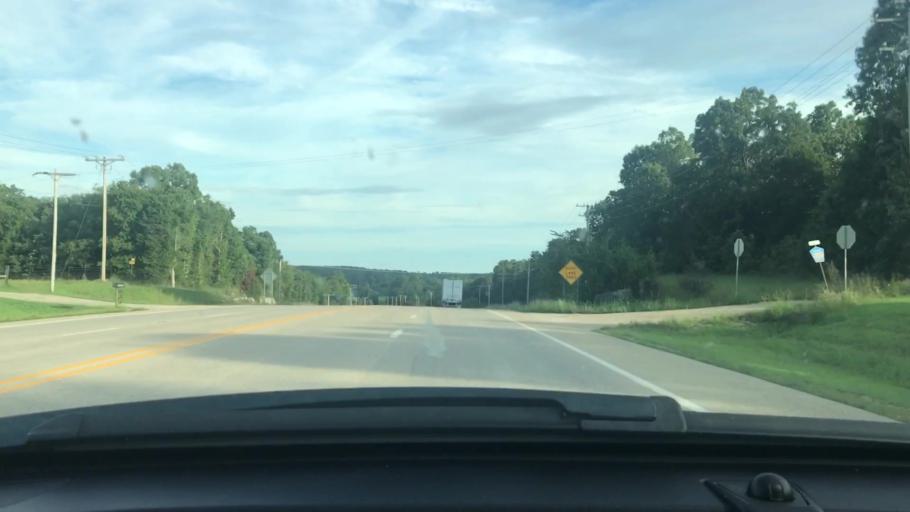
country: US
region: Arkansas
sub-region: Lawrence County
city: Hoxie
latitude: 36.1274
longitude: -91.1564
